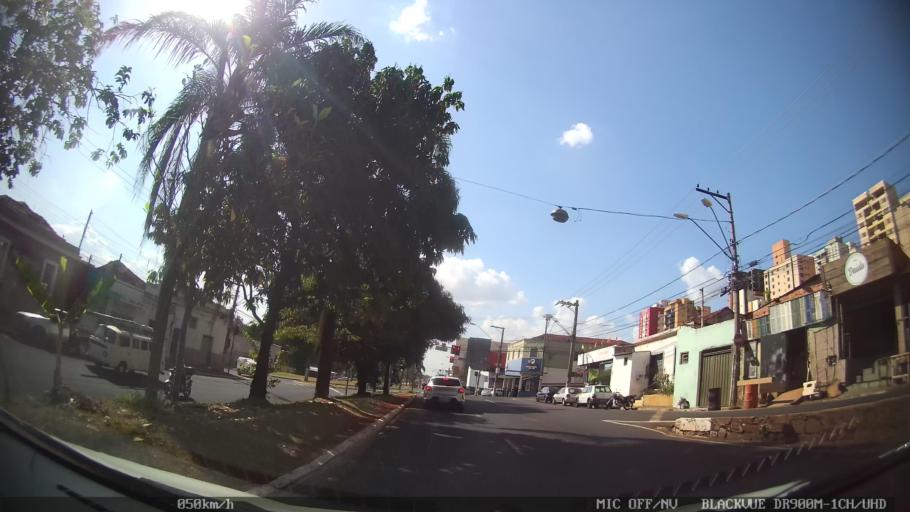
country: BR
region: Sao Paulo
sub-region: Ribeirao Preto
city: Ribeirao Preto
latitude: -21.1792
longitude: -47.8167
